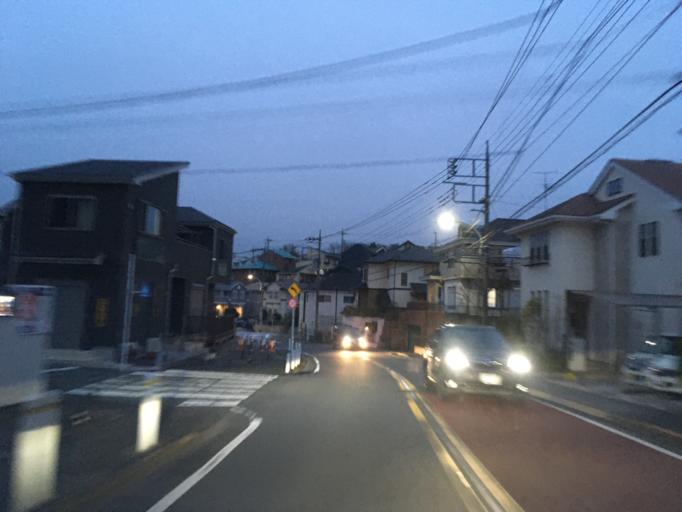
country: JP
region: Tokyo
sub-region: Machida-shi
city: Machida
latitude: 35.5198
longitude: 139.4783
